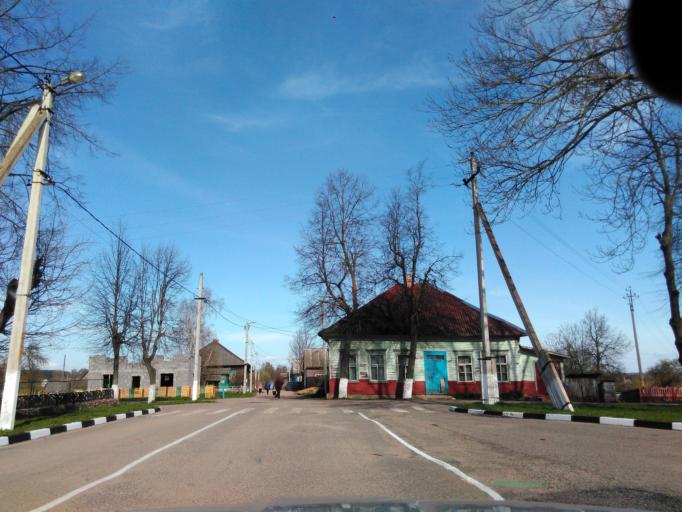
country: BY
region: Vitebsk
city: Chashniki
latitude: 54.8644
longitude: 29.1616
